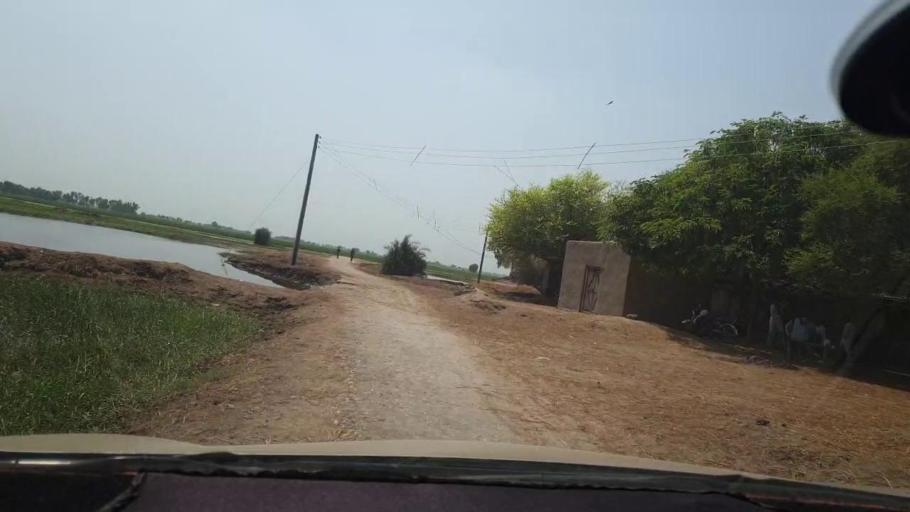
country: PK
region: Sindh
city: Kambar
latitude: 27.6566
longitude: 67.9314
